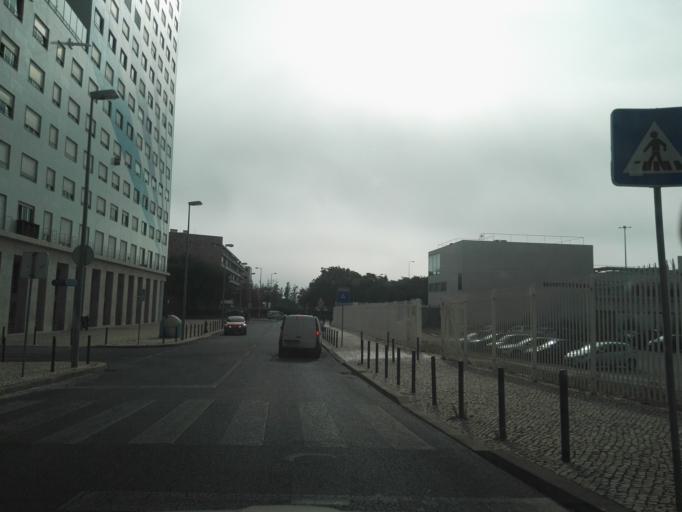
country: PT
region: Lisbon
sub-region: Loures
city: Moscavide
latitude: 38.7555
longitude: -9.0980
